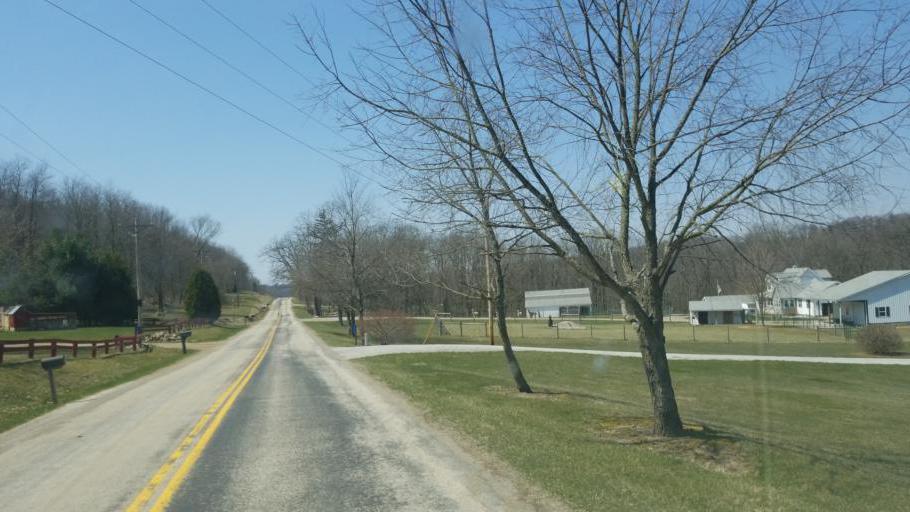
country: US
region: Ohio
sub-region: Ashland County
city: Loudonville
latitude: 40.7282
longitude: -82.2635
